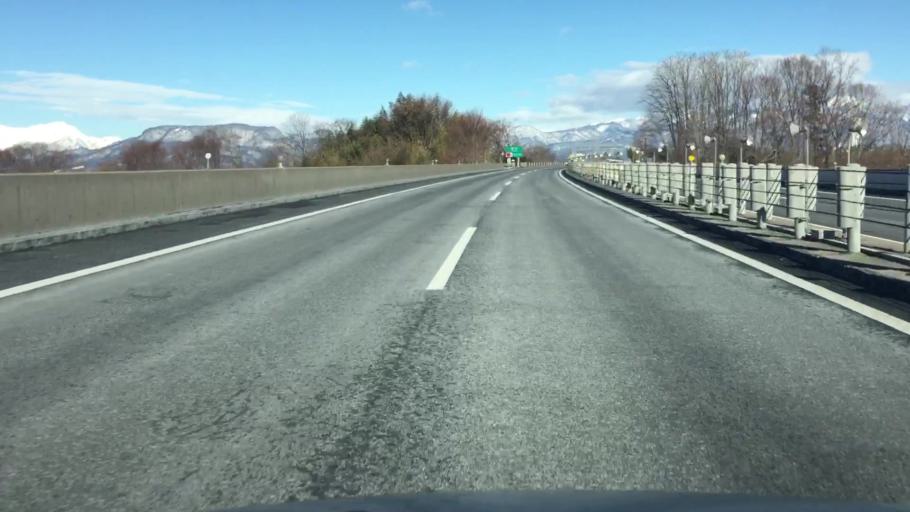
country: JP
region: Gunma
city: Numata
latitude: 36.6045
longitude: 139.0626
